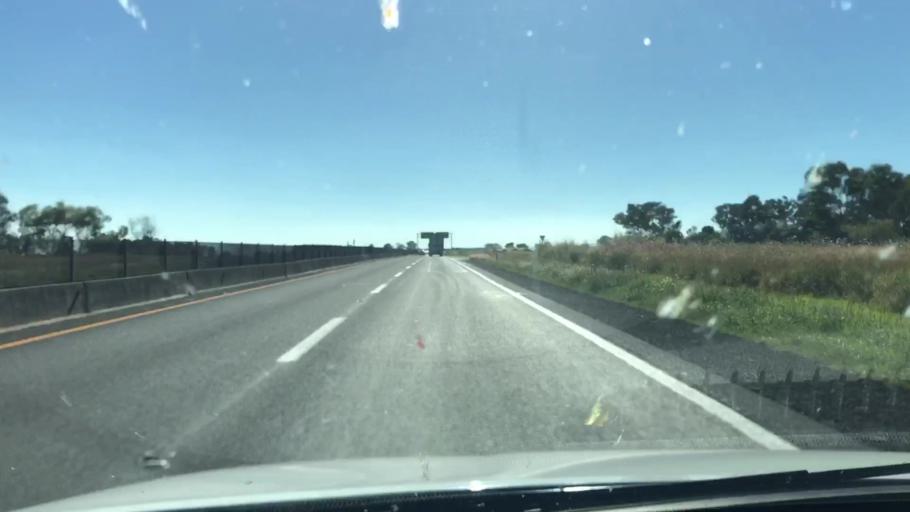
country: MX
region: Jalisco
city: Tepatitlan de Morelos
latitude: 20.8971
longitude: -102.7050
